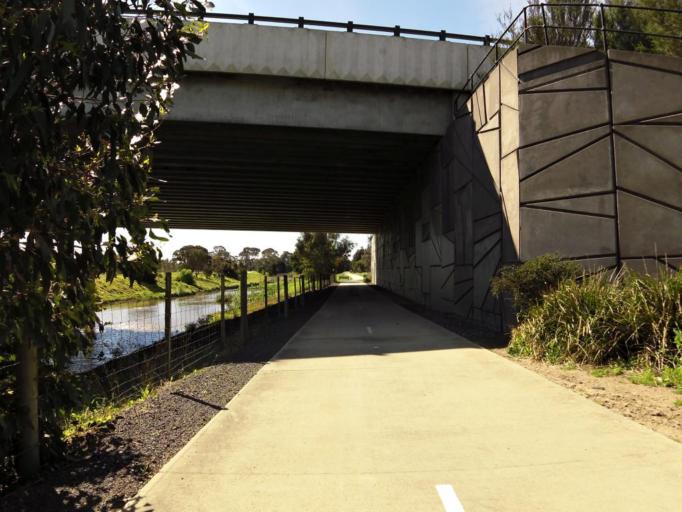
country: AU
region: Victoria
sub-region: Greater Dandenong
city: Dandenong
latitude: -38.0018
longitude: 145.1935
